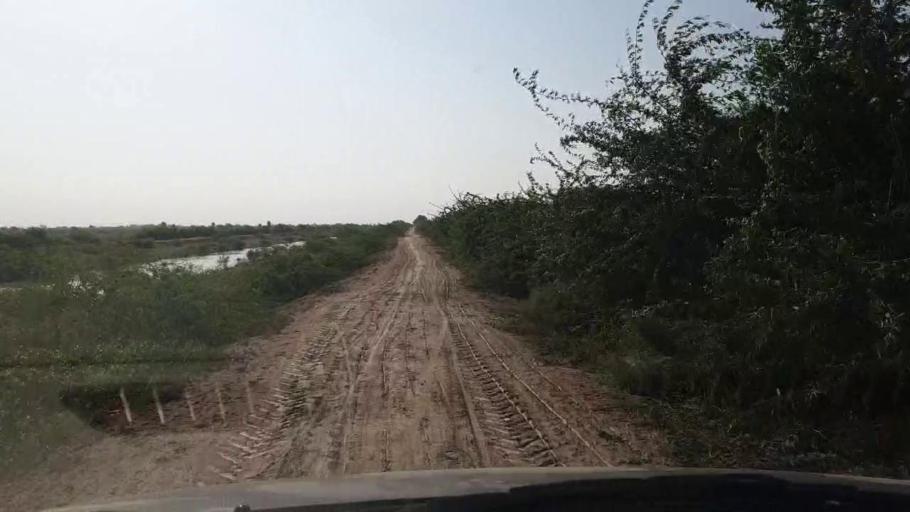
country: PK
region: Sindh
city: Kadhan
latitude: 24.5916
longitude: 69.0764
